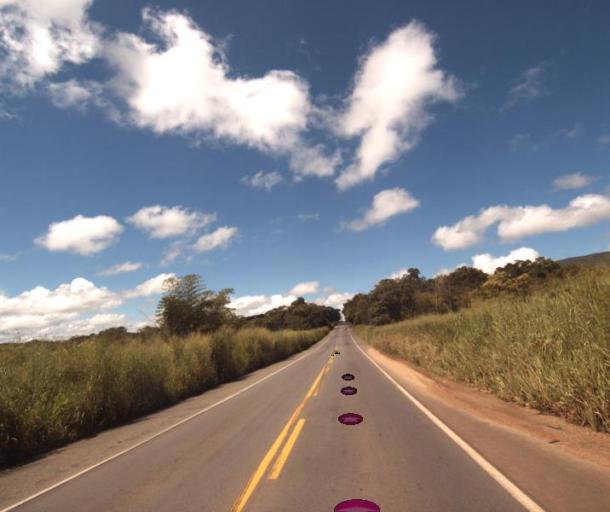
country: BR
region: Goias
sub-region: Jaragua
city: Jaragua
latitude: -15.7879
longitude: -49.3028
